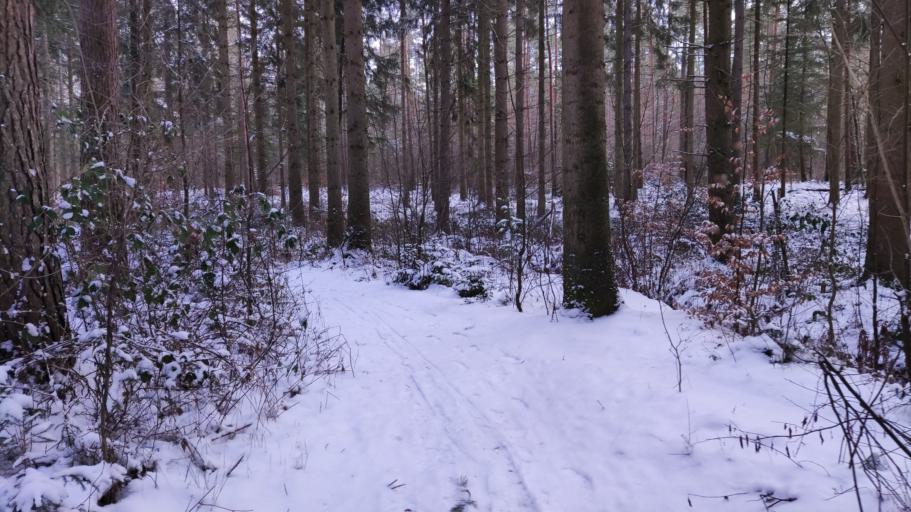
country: DE
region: Lower Saxony
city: Deutsch Evern
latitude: 53.2272
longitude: 10.4308
